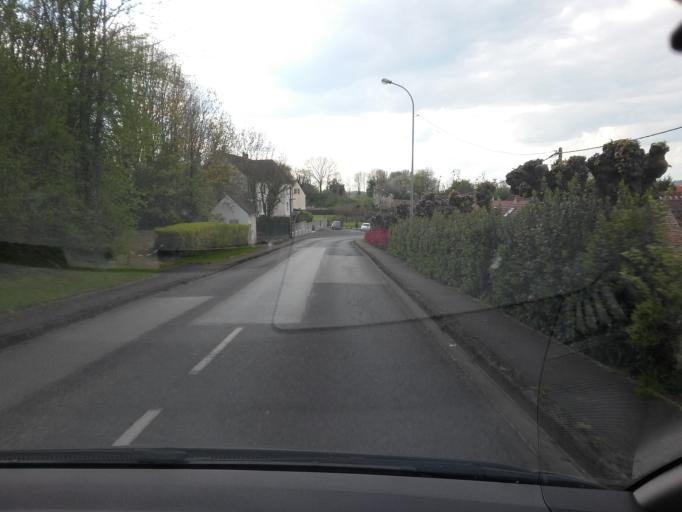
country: FR
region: Picardie
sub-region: Departement de l'Oise
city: Grandfresnoy
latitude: 49.3728
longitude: 2.6507
